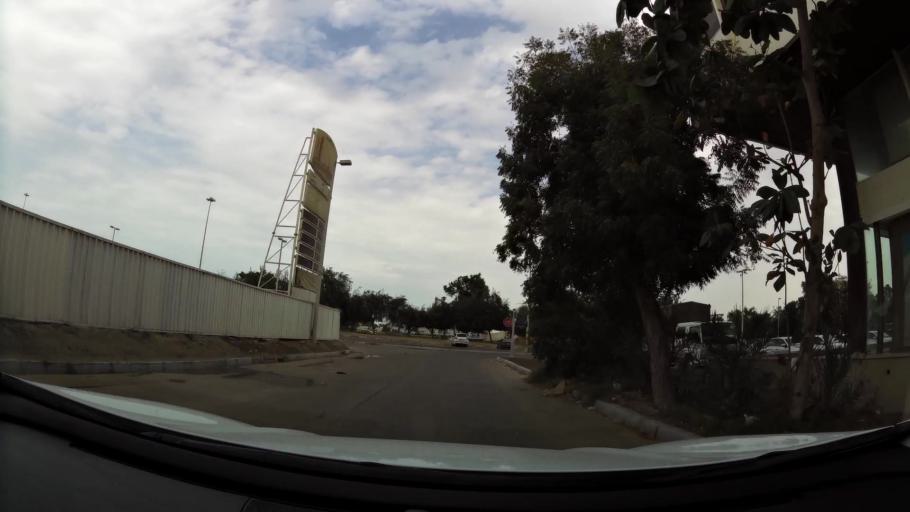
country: AE
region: Abu Dhabi
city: Abu Dhabi
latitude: 24.4243
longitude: 54.4511
